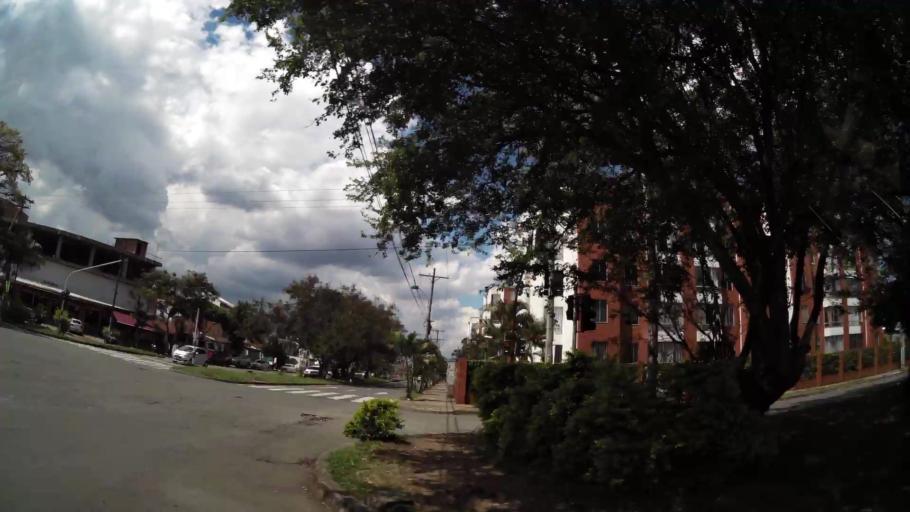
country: CO
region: Valle del Cauca
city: Cali
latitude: 3.3837
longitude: -76.5201
